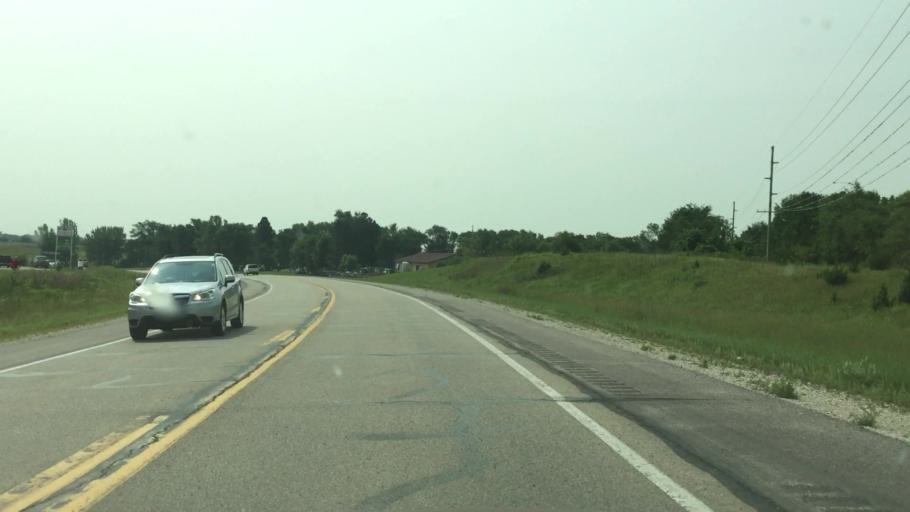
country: US
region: Iowa
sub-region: Dickinson County
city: Milford
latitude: 43.3455
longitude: -95.1794
